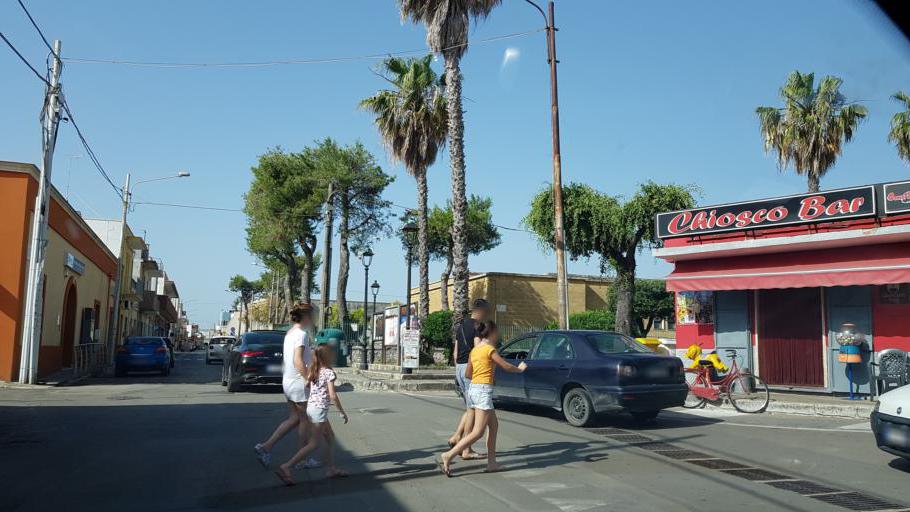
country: IT
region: Apulia
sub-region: Provincia di Brindisi
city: San Pancrazio Salentino
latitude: 40.4167
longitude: 17.8400
